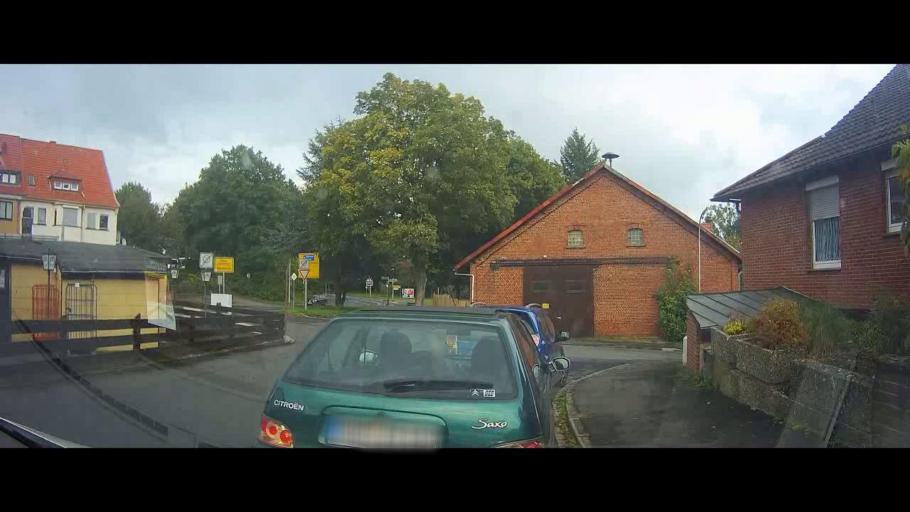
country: DE
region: Lower Saxony
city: Uslar
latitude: 51.6411
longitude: 9.6573
